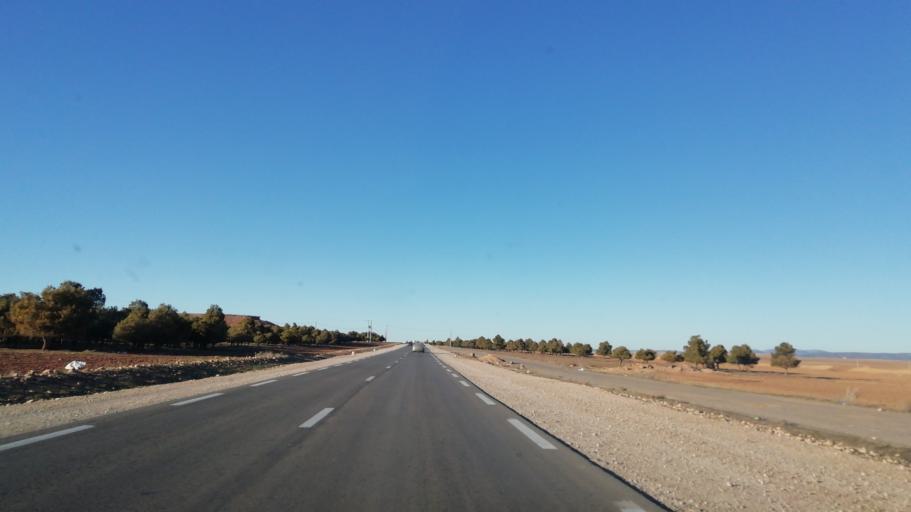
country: DZ
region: Tlemcen
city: Sebdou
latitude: 34.4977
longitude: -1.2763
